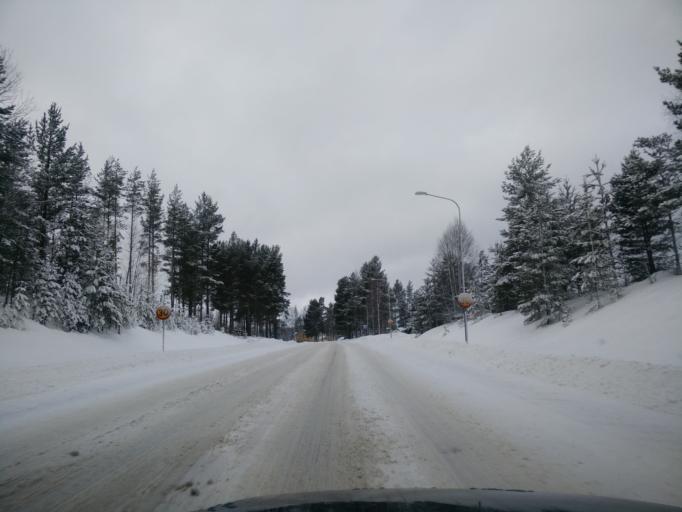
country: SE
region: Vaesternorrland
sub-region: Ange Kommun
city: Ange
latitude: 62.4962
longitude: 15.4791
